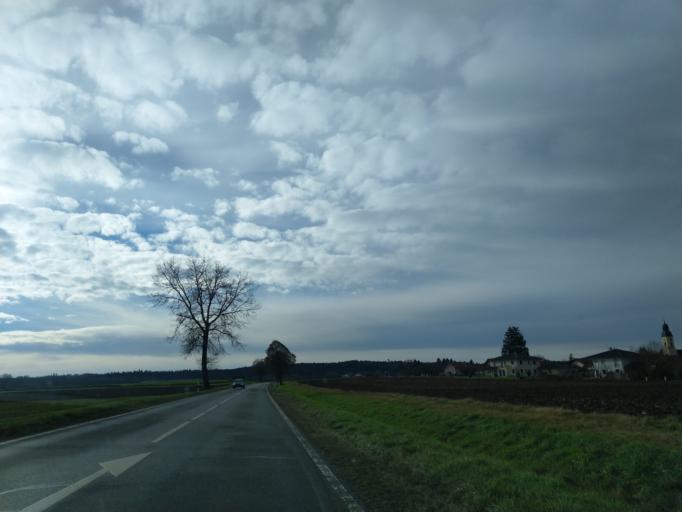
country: DE
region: Bavaria
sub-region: Lower Bavaria
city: Osterhofen
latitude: 48.6606
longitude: 12.9834
